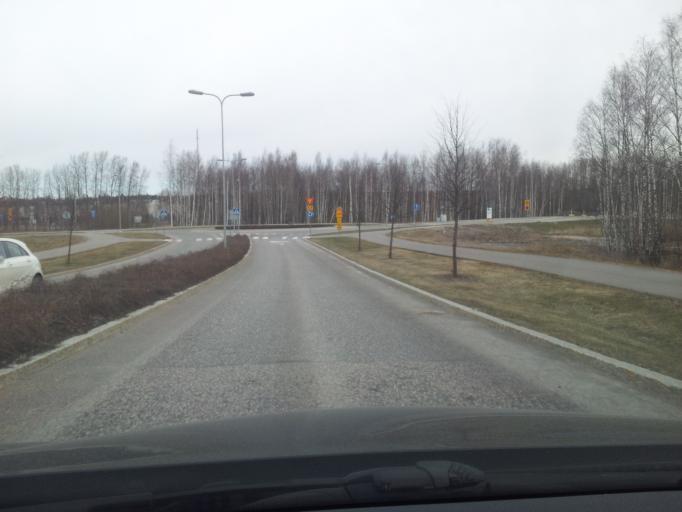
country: FI
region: Uusimaa
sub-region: Helsinki
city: Teekkarikylae
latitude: 60.2107
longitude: 24.8317
